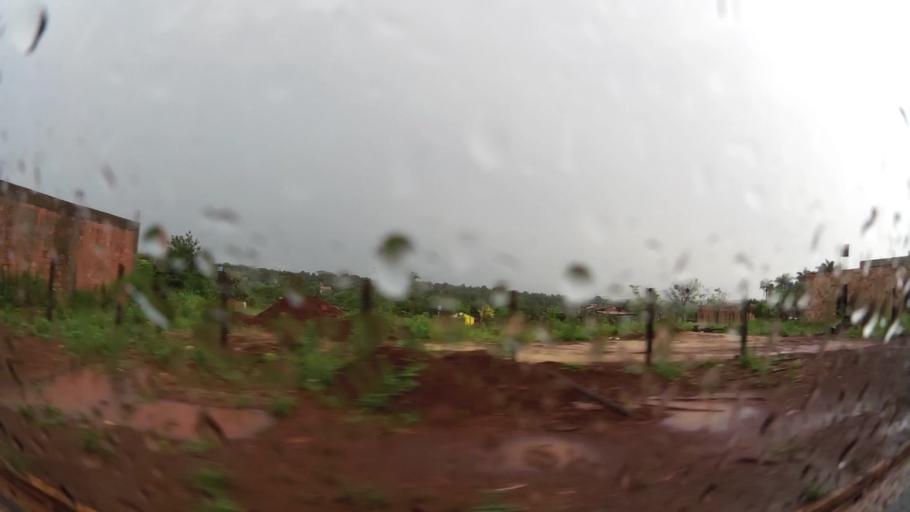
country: PY
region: Alto Parana
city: Presidente Franco
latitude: -25.5523
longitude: -54.6666
